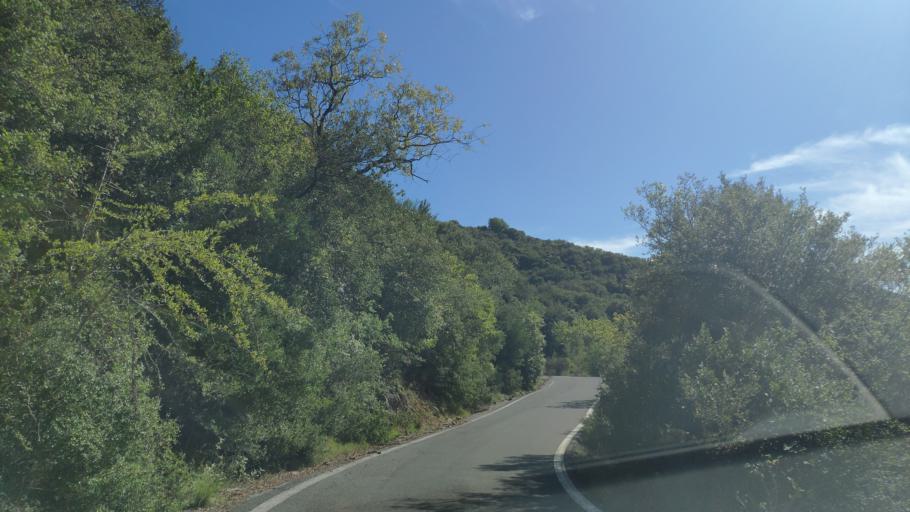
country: GR
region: Peloponnese
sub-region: Nomos Arkadias
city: Dimitsana
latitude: 37.5376
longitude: 22.0478
